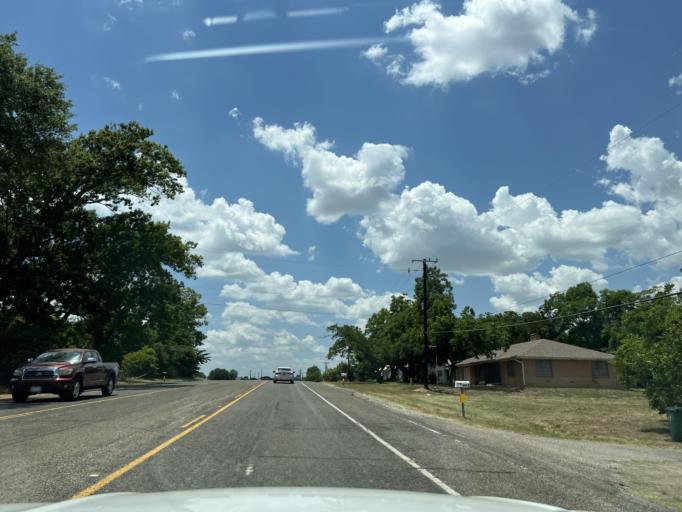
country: US
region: Texas
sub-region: Washington County
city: Brenham
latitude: 30.1476
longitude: -96.3793
